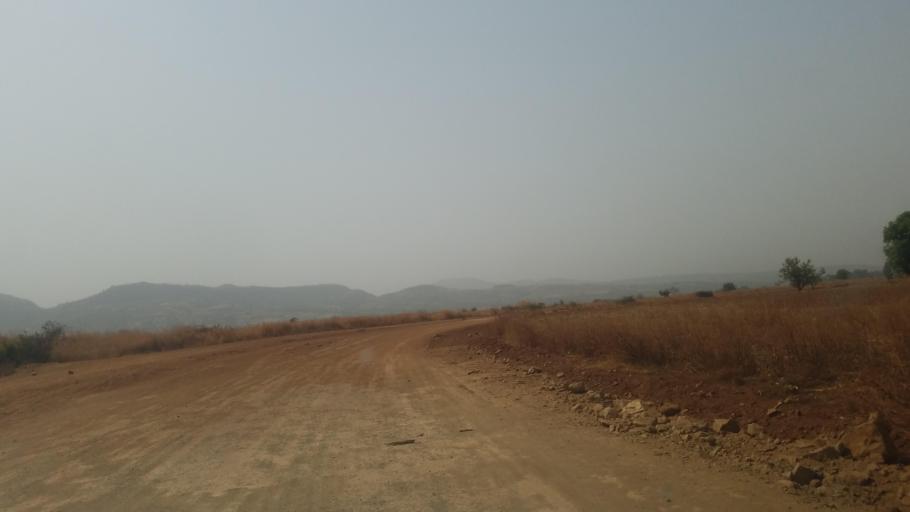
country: ET
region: Amhara
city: Bure
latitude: 10.8998
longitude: 36.4658
